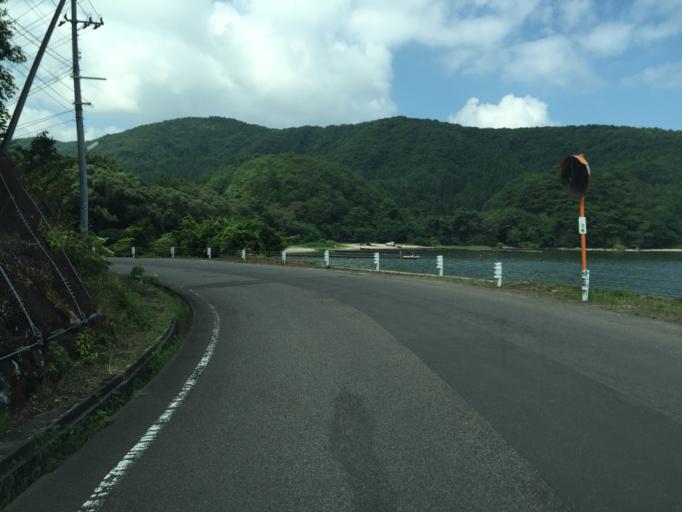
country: JP
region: Fukushima
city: Inawashiro
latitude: 37.4134
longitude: 140.1129
